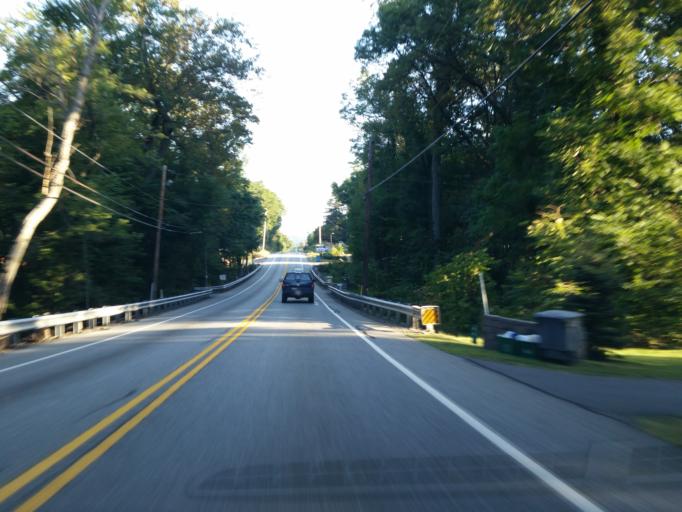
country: US
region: Pennsylvania
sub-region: Lancaster County
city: Quarryville
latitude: 39.8973
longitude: -76.2406
